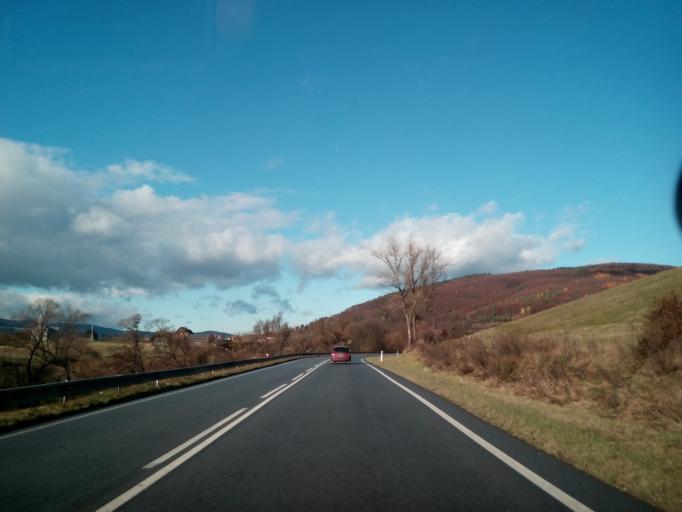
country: SK
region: Presovsky
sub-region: Okres Bardejov
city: Bardejov
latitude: 49.2525
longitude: 21.2524
